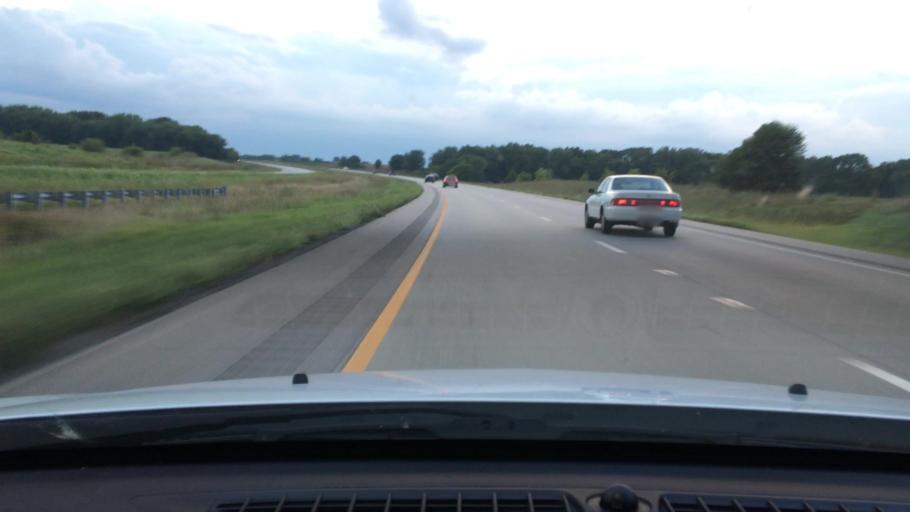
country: US
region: Illinois
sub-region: Sangamon County
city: New Berlin
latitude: 39.7511
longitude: -89.7997
